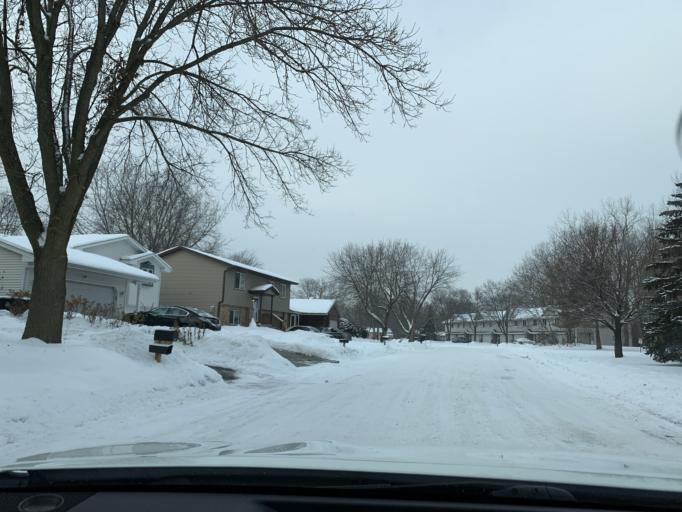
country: US
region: Minnesota
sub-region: Anoka County
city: Coon Rapids
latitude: 45.1598
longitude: -93.2901
